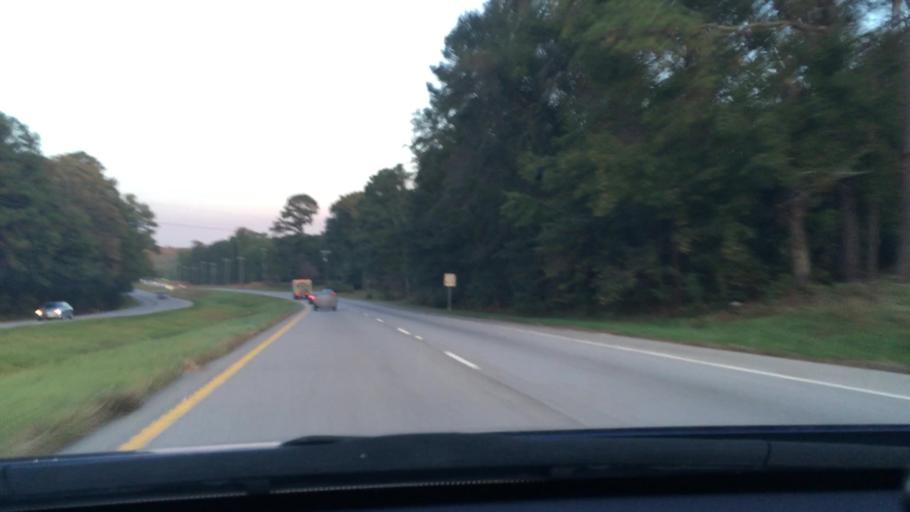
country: US
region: South Carolina
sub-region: Richland County
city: Gadsden
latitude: 33.9427
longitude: -80.7713
